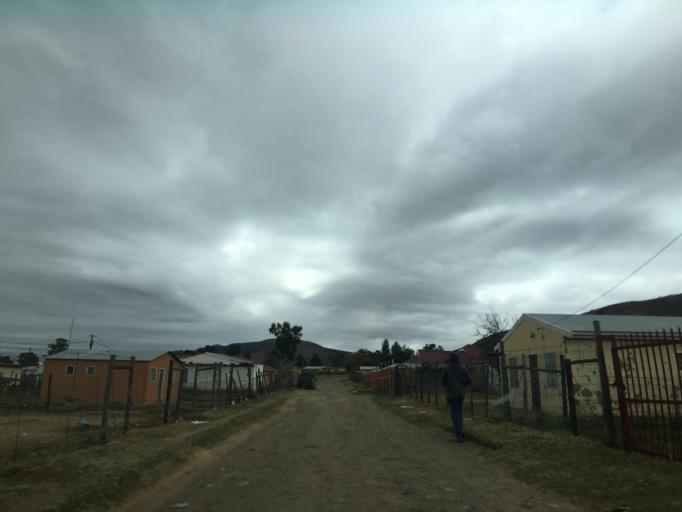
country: ZA
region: Eastern Cape
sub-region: Chris Hani District Municipality
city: Cala
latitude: -31.5327
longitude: 27.7011
